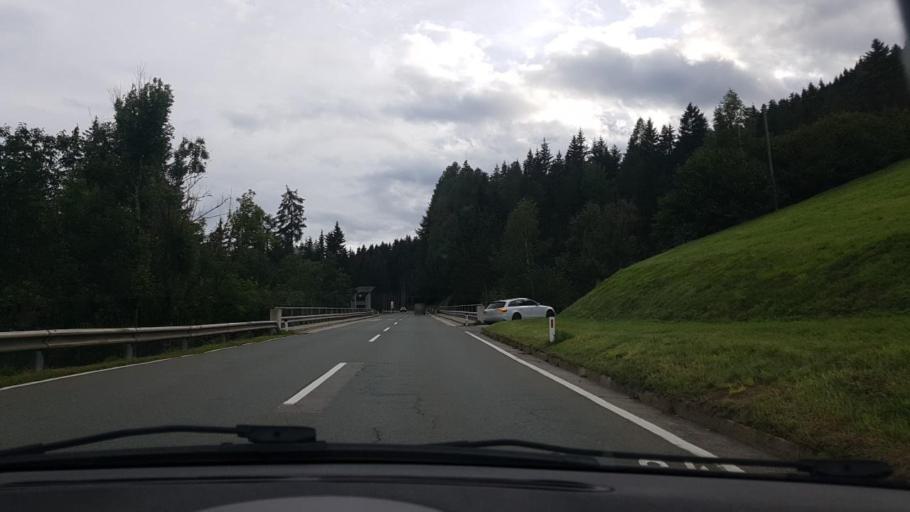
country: AT
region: Carinthia
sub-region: Politischer Bezirk Spittal an der Drau
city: Winklern
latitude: 46.8661
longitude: 12.8685
